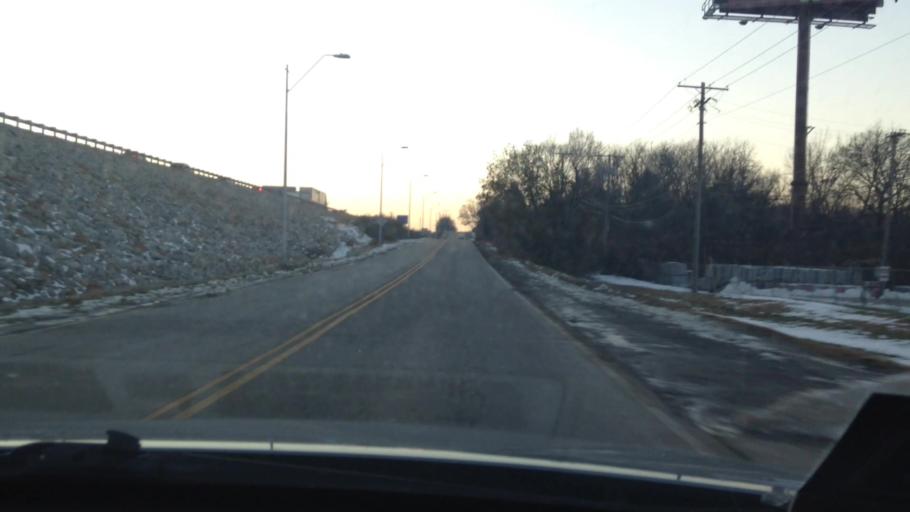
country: US
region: Kansas
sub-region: Johnson County
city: Leawood
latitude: 38.9403
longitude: -94.5682
